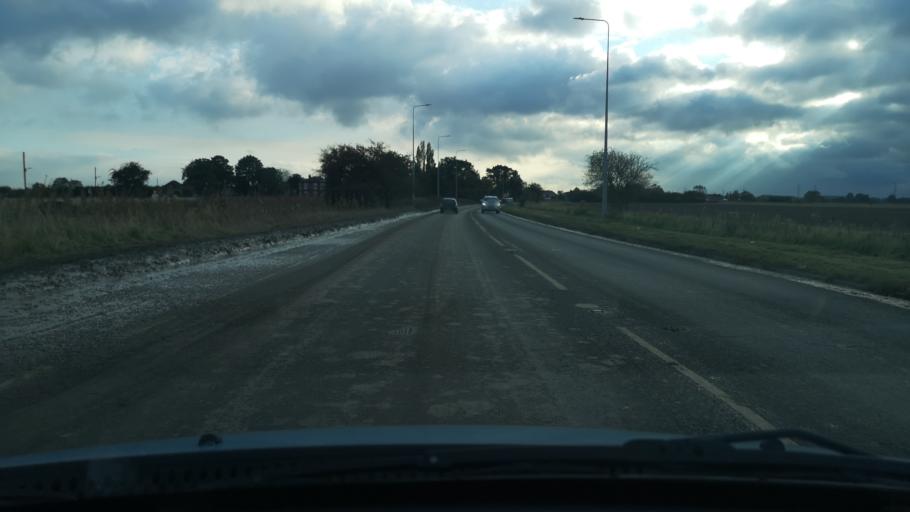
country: GB
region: England
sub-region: North Lincolnshire
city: Gunness
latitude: 53.5824
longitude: -0.7380
